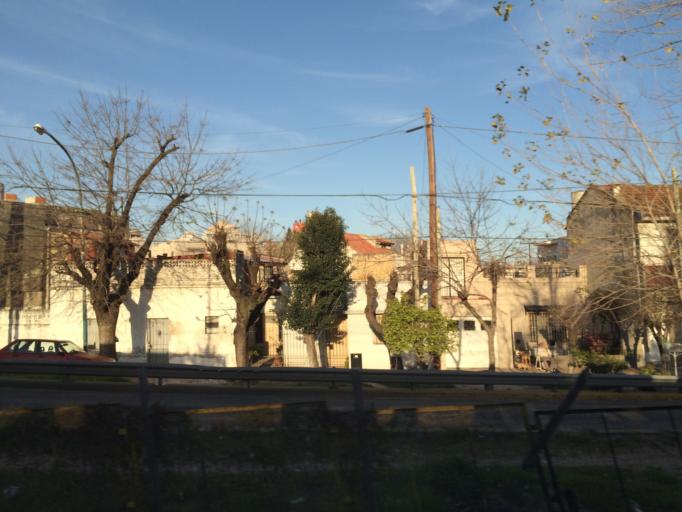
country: AR
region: Buenos Aires
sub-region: Partido de Lanus
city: Lanus
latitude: -34.7129
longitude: -58.3920
